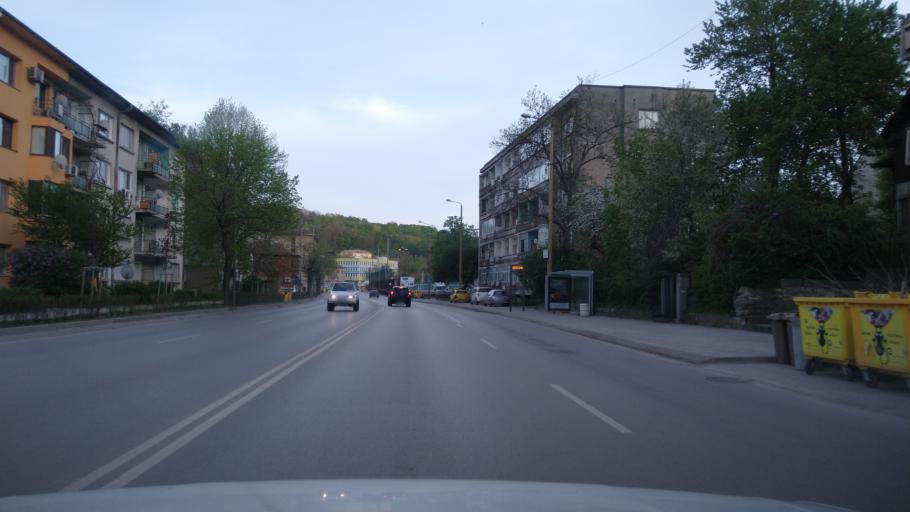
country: BG
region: Gabrovo
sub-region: Obshtina Gabrovo
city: Gabrovo
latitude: 42.8628
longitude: 25.3199
